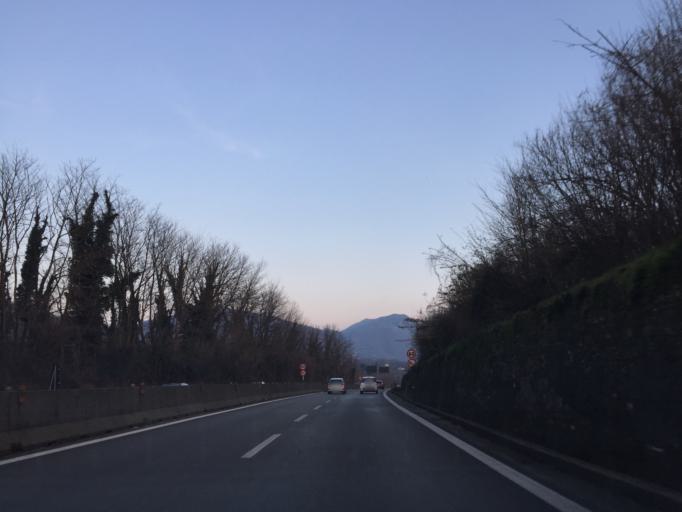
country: IT
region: Campania
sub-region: Provincia di Avellino
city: Atripalda
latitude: 40.9128
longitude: 14.8238
